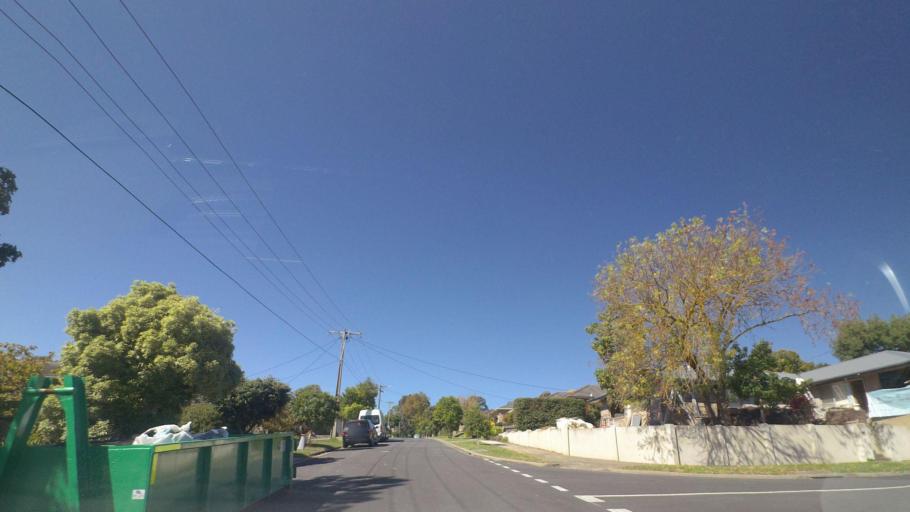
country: AU
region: Victoria
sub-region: Manningham
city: Donvale
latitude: -37.7993
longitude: 145.1714
